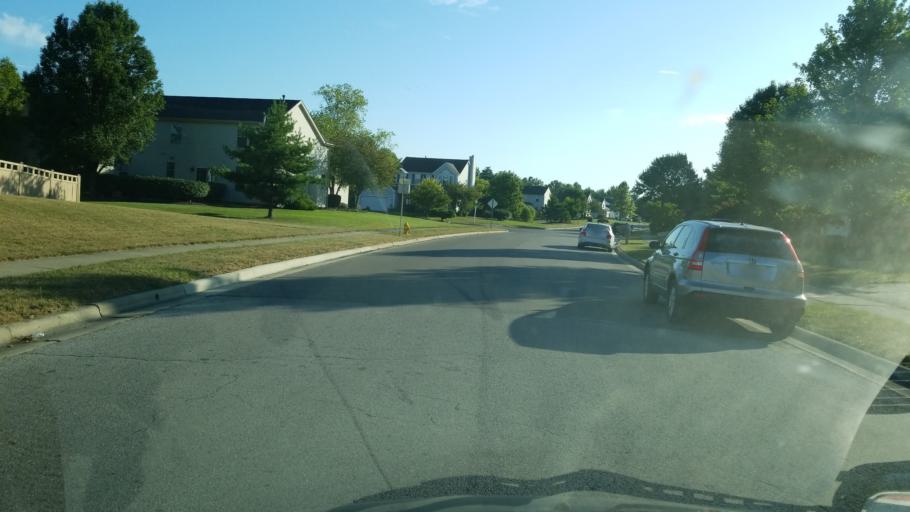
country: US
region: Ohio
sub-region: Delaware County
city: Lewis Center
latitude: 40.1681
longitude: -83.0035
